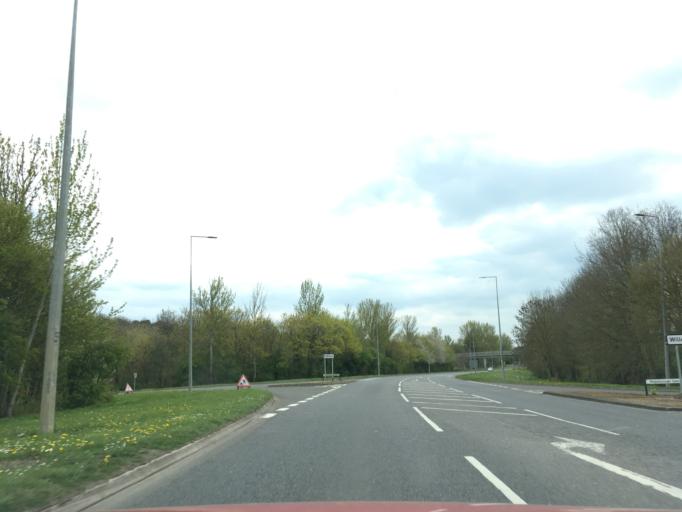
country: GB
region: England
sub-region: Milton Keynes
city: Newport Pagnell
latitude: 52.0603
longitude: -0.7302
